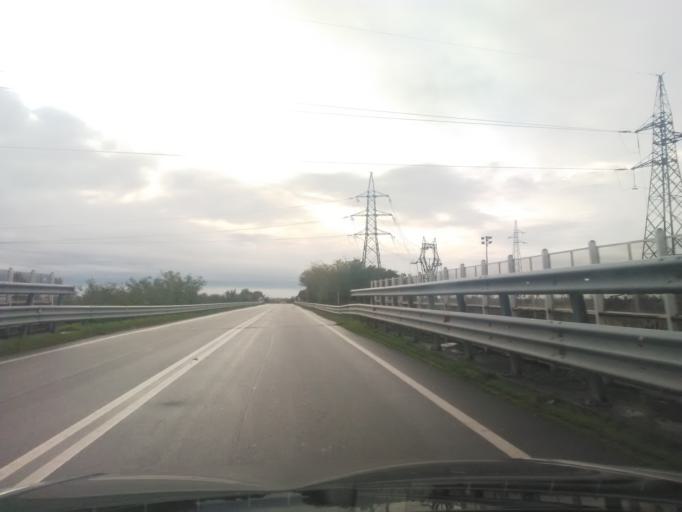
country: IT
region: Piedmont
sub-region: Provincia di Vercelli
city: Santhia
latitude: 45.3663
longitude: 8.1856
